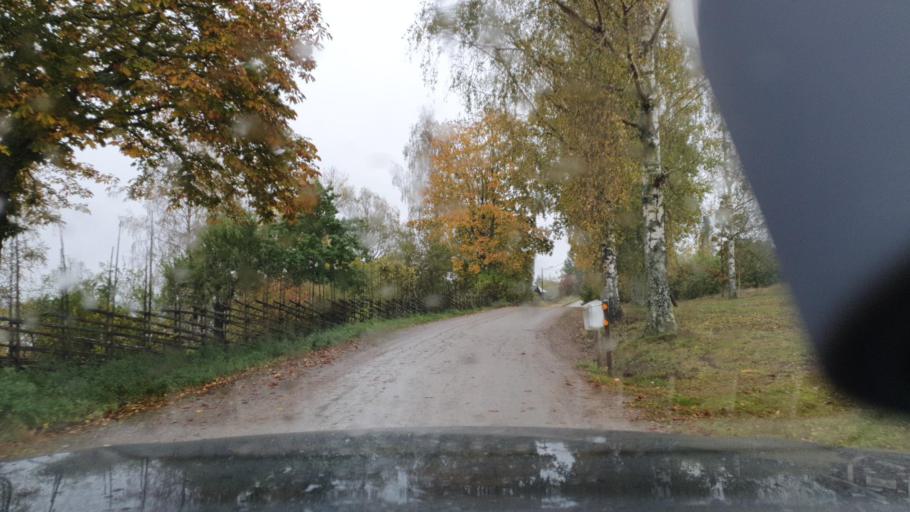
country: SE
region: Vaermland
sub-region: Karlstads Kommun
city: Edsvalla
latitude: 59.6099
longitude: 12.9157
